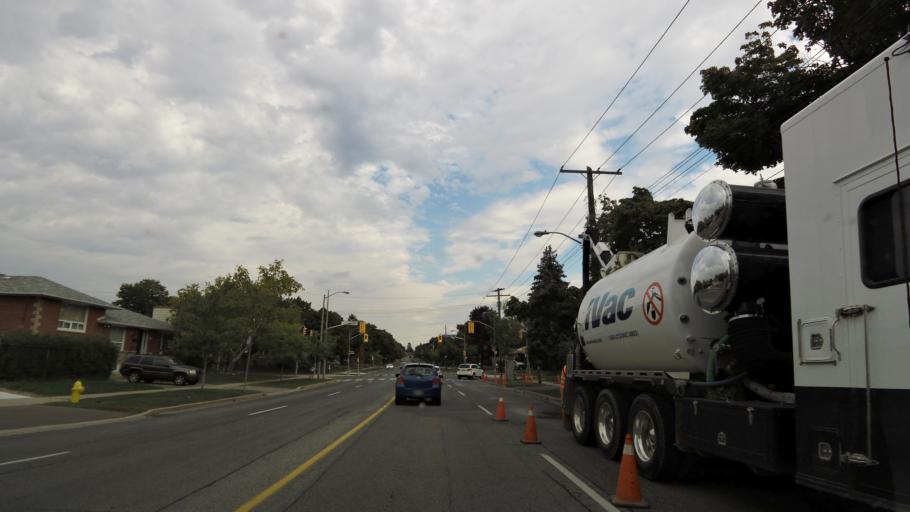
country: CA
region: Ontario
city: Etobicoke
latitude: 43.6889
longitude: -79.5416
